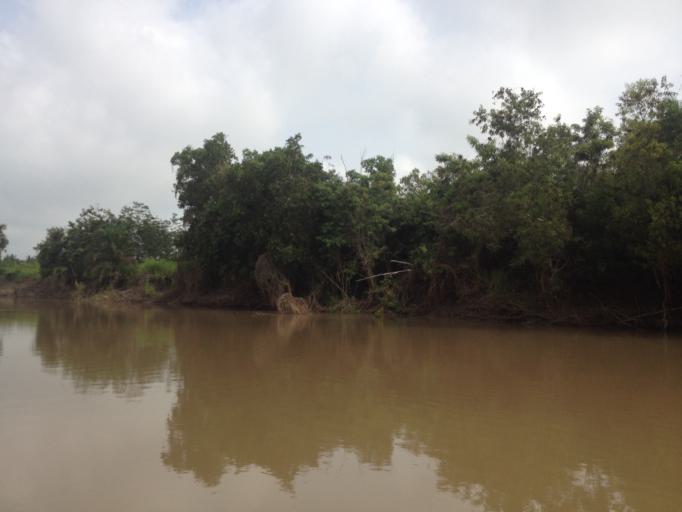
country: BJ
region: Mono
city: Come
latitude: 6.3920
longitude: 1.7734
